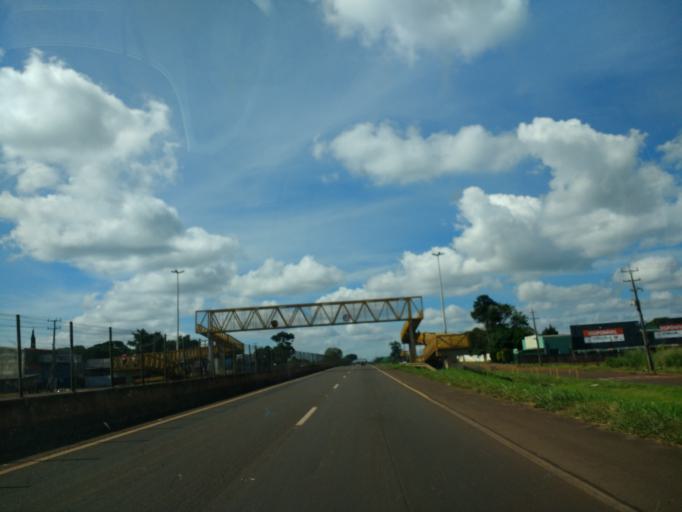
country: BR
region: Parana
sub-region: Paicandu
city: Paicandu
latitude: -23.4614
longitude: -52.0370
